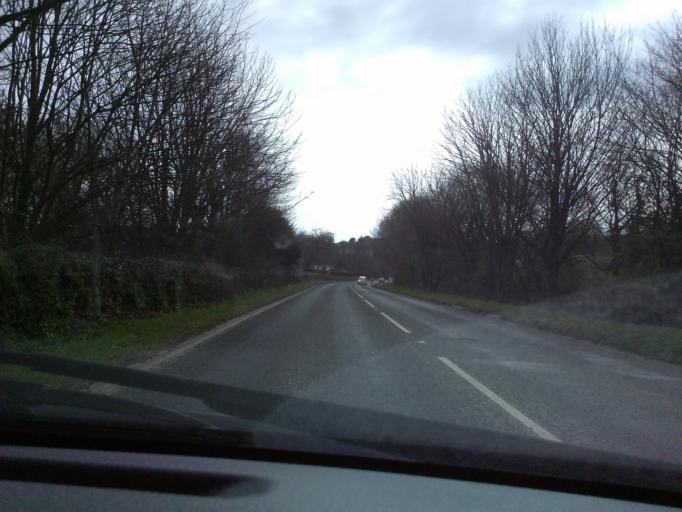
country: GB
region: England
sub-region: Cornwall
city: Penzance
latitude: 50.1197
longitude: -5.5519
